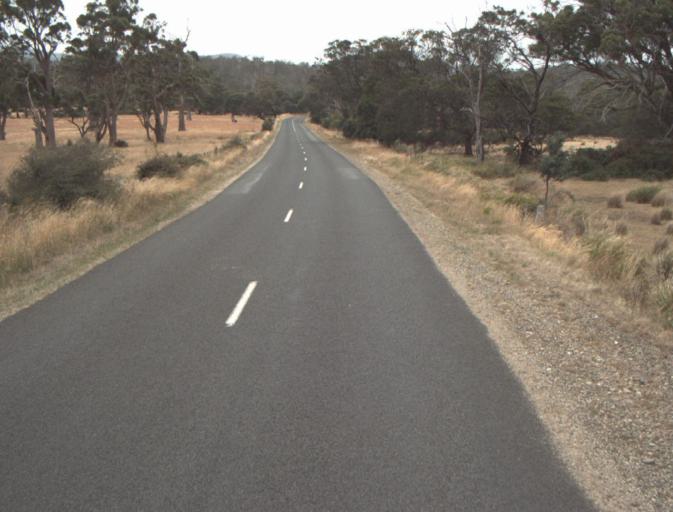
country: AU
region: Tasmania
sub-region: Northern Midlands
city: Evandale
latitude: -41.5126
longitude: 147.3094
